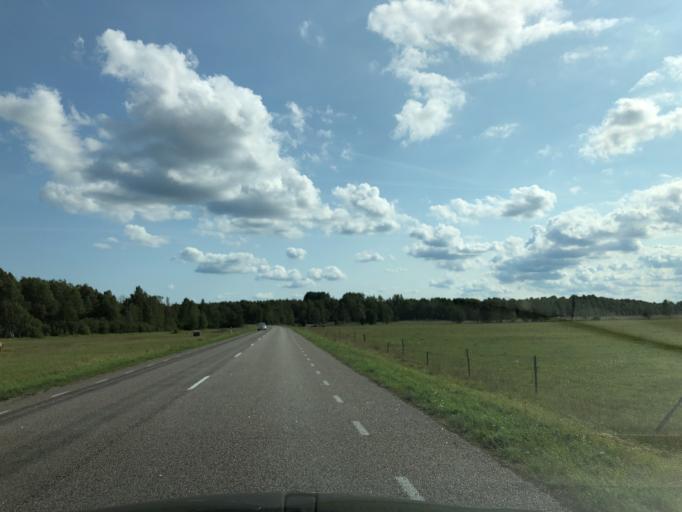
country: EE
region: Hiiumaa
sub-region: Kaerdla linn
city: Kardla
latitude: 58.7227
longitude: 22.5624
